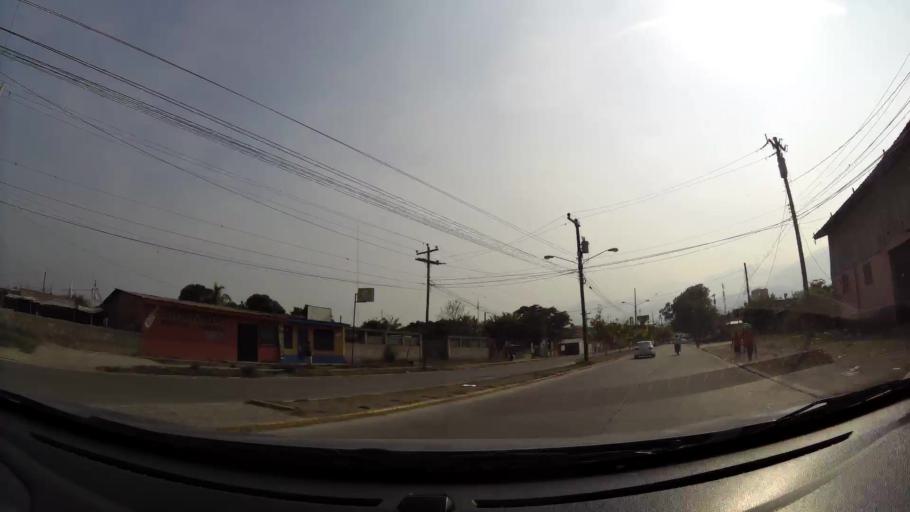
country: HN
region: Comayagua
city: Comayagua
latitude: 14.4462
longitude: -87.6352
